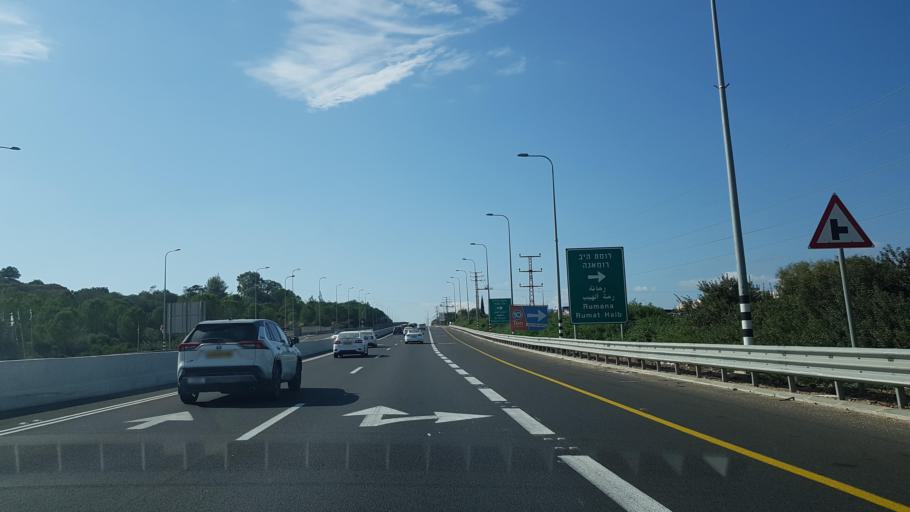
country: IL
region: Northern District
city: Rumat Heib
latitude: 32.7667
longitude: 35.3138
